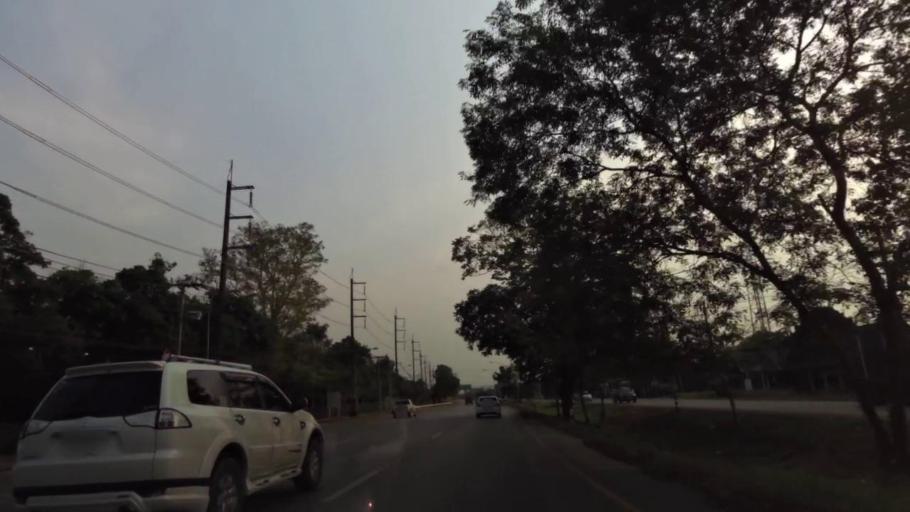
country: TH
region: Chanthaburi
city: Khlung
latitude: 12.5095
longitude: 102.1693
